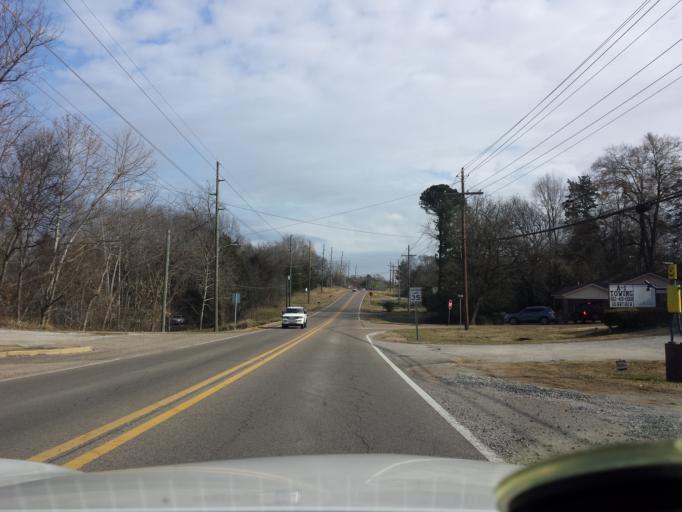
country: US
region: Mississippi
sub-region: Oktibbeha County
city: Starkville
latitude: 33.4652
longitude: -88.8267
